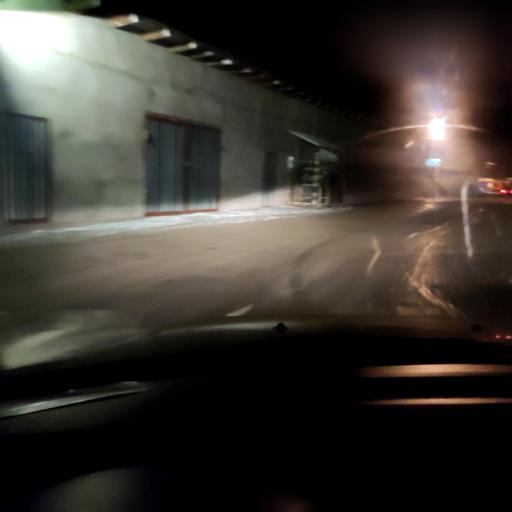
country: RU
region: Samara
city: Zhigulevsk
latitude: 53.5216
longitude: 49.4768
